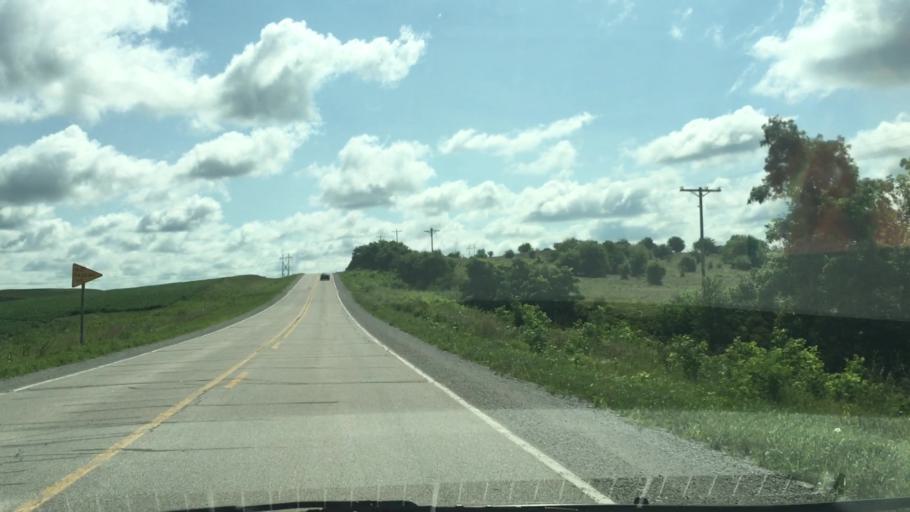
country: US
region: Iowa
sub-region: Johnson County
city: Solon
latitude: 41.8312
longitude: -91.4905
